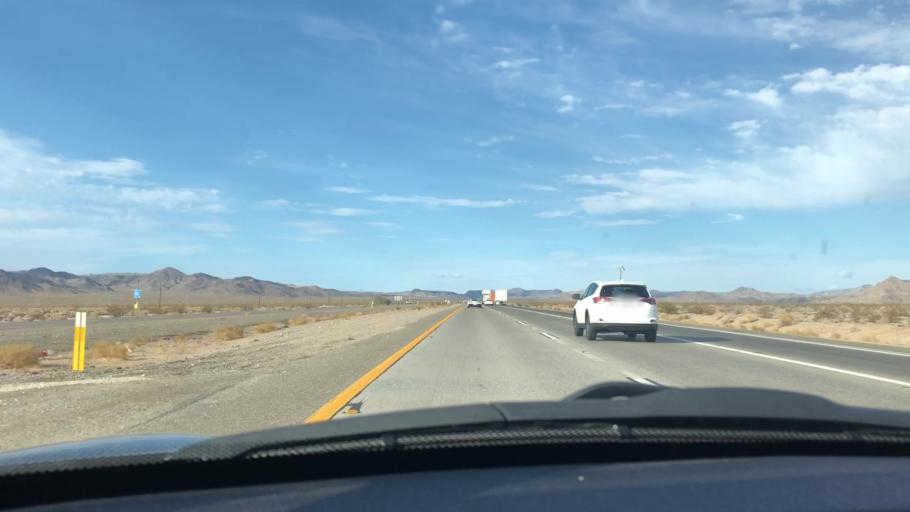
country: US
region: Nevada
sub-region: Clark County
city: Sandy Valley
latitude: 35.3114
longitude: -116.0022
